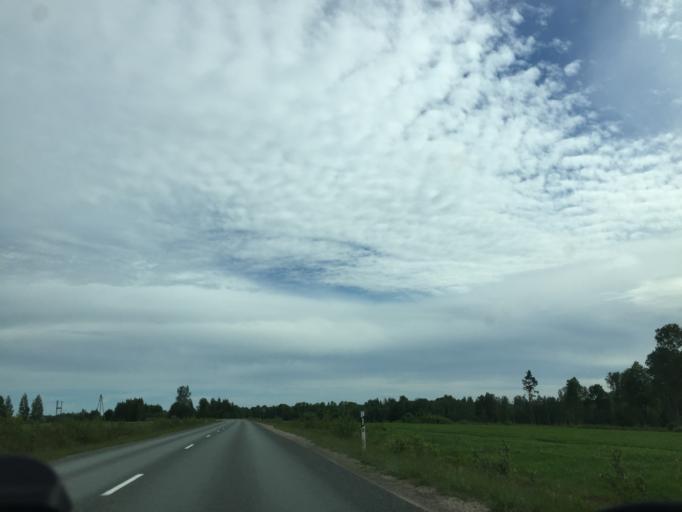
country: LV
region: Beverina
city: Murmuiza
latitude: 57.4641
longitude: 25.4154
